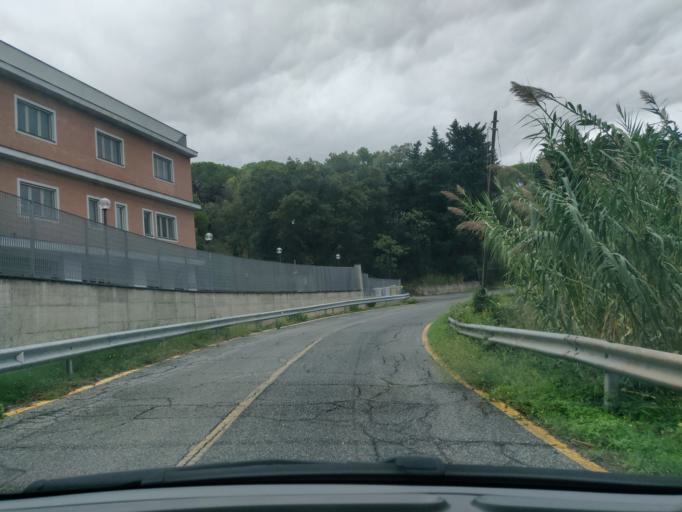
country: IT
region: Latium
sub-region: Citta metropolitana di Roma Capitale
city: Aurelia
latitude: 42.1338
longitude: 11.8406
